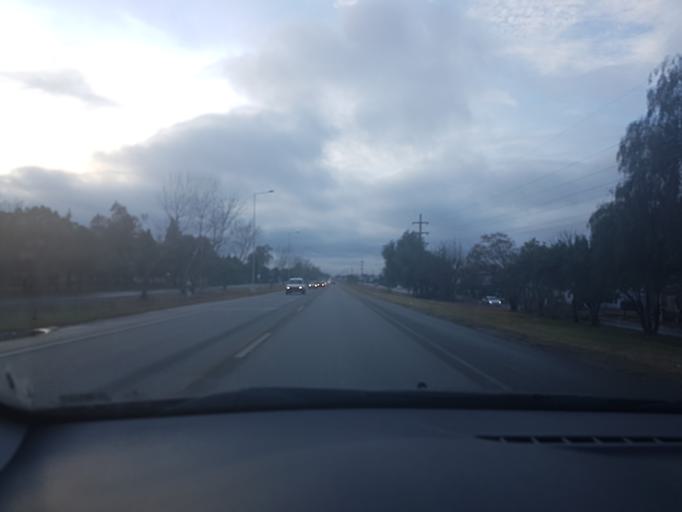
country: AR
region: Cordoba
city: Villa Allende
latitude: -31.3008
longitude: -64.2736
